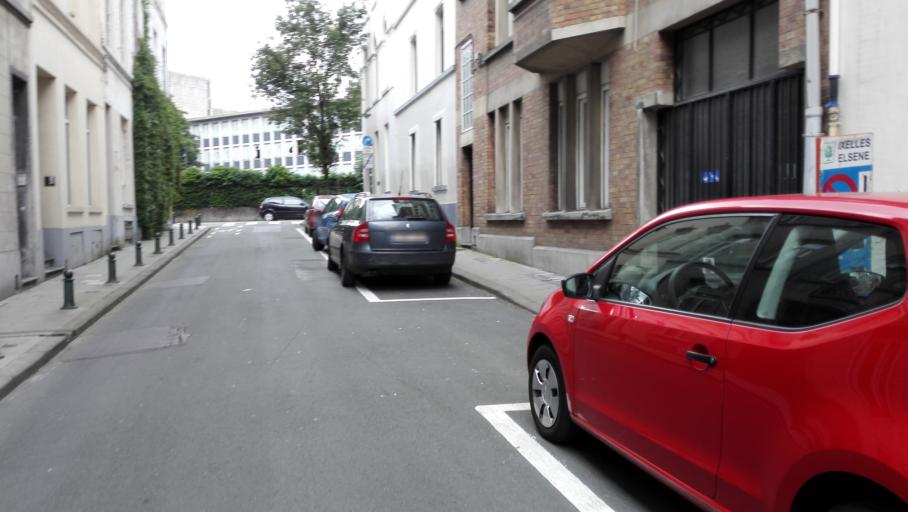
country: BE
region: Brussels Capital
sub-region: Bruxelles-Capitale
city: Brussels
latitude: 50.8331
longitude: 4.3625
